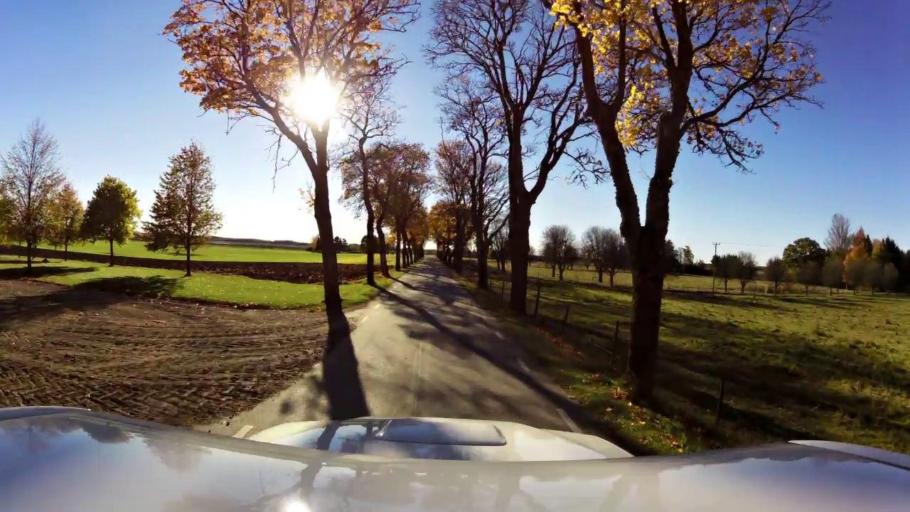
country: SE
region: OEstergoetland
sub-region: Linkopings Kommun
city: Ljungsbro
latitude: 58.5089
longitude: 15.4171
